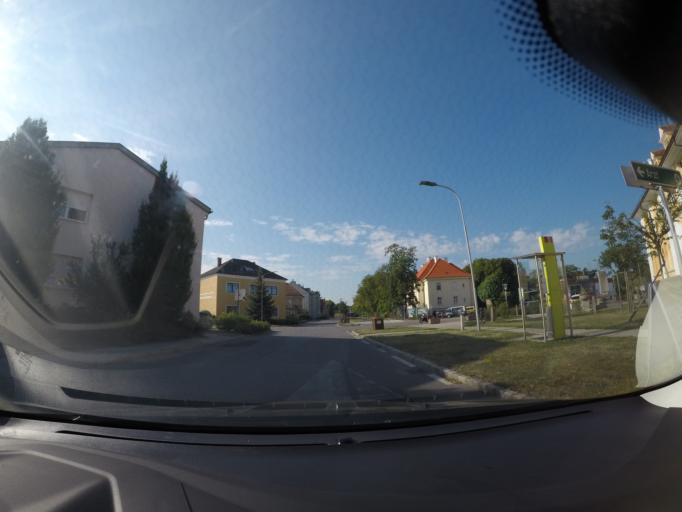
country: AT
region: Lower Austria
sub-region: Politischer Bezirk Baden
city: Tattendorf
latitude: 47.9270
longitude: 16.3025
